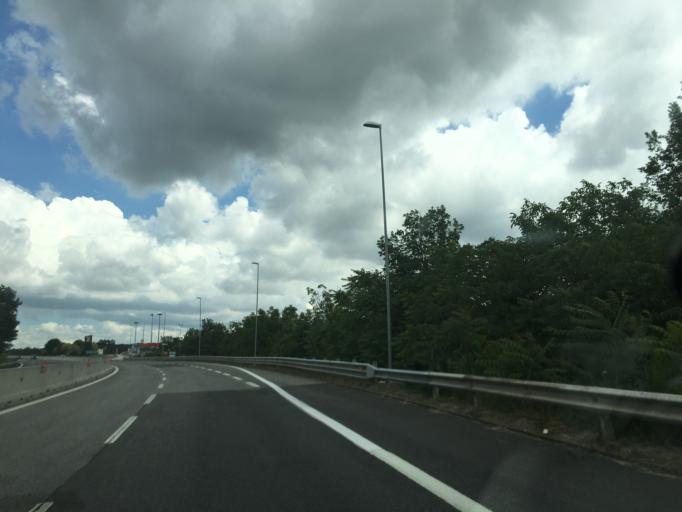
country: IT
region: Campania
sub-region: Provincia di Avellino
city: Passo di Mirabella-Pianopantano
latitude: 41.0617
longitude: 15.0102
